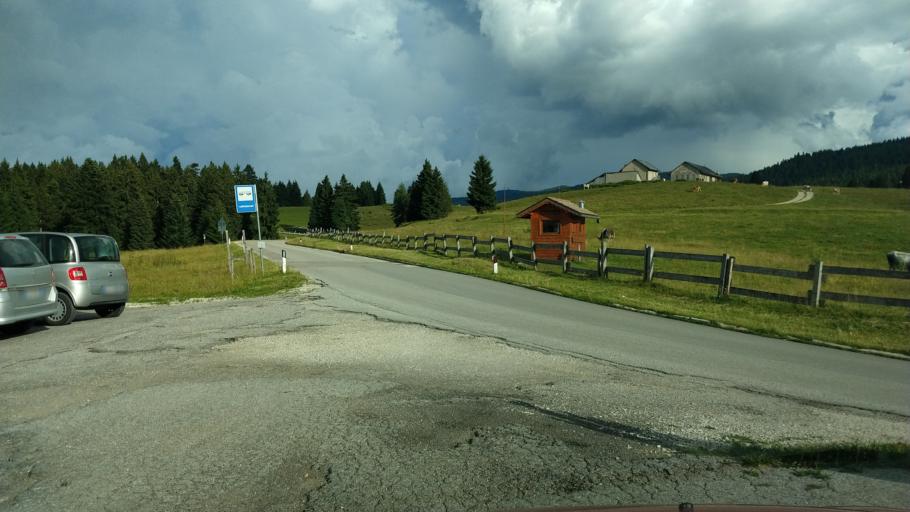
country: IT
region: Veneto
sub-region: Provincia di Vicenza
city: Lastebasse
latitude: 45.9133
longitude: 11.2342
